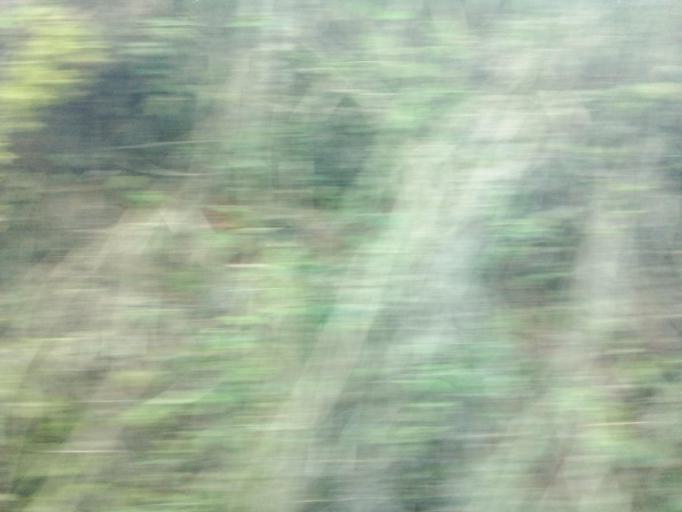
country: BR
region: Minas Gerais
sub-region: Rio Piracicaba
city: Rio Piracicaba
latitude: -19.8961
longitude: -43.1425
